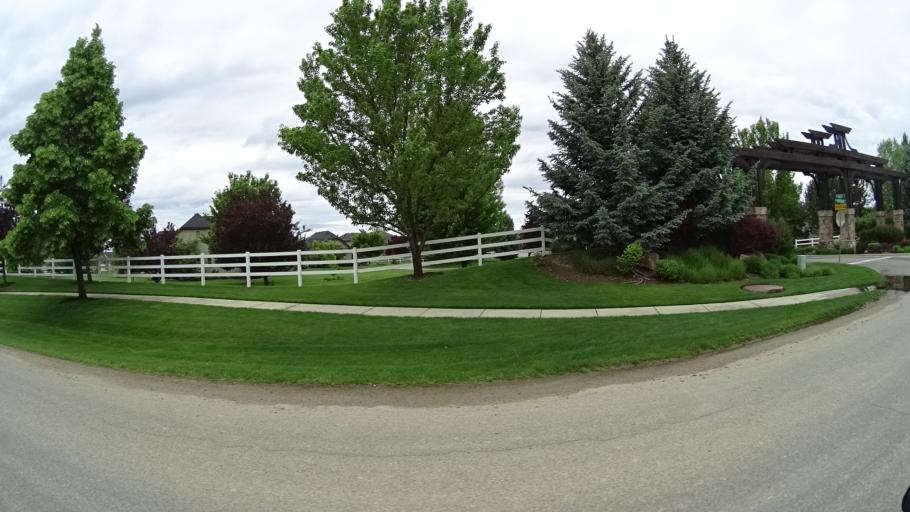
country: US
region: Idaho
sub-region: Ada County
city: Eagle
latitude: 43.7152
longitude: -116.3935
